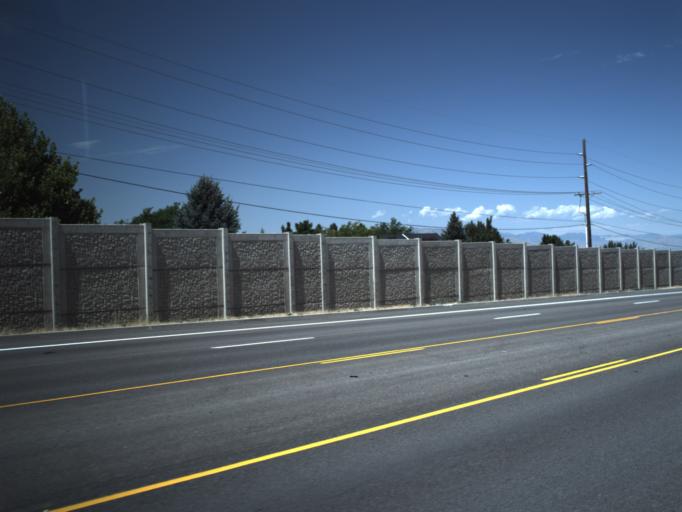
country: US
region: Utah
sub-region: Utah County
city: Spanish Fork
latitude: 40.1122
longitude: -111.6339
